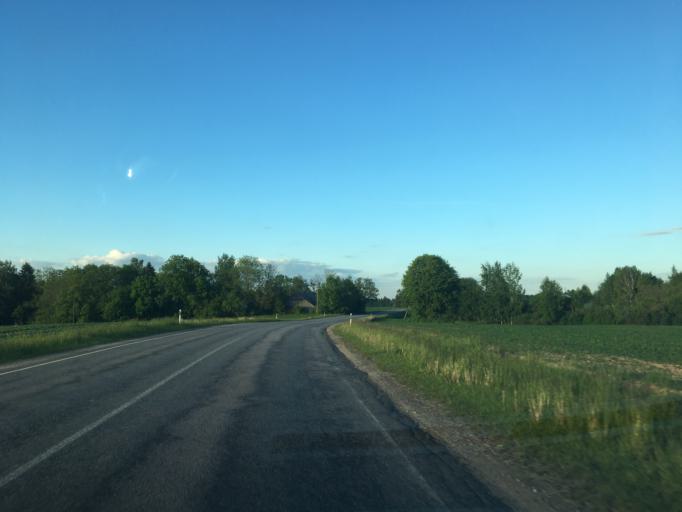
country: EE
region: Tartu
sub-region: Noo vald
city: Noo
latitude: 58.2123
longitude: 26.5929
